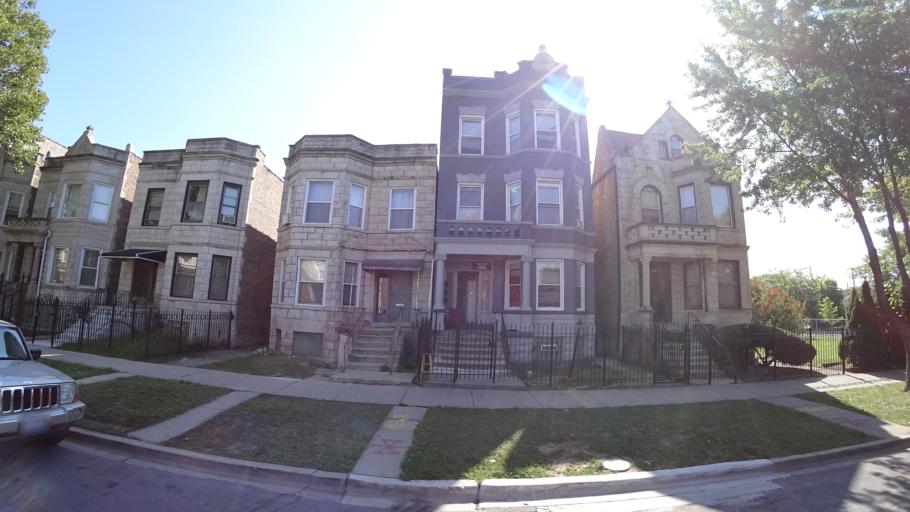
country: US
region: Illinois
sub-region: Cook County
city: Cicero
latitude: 41.8648
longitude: -87.7227
